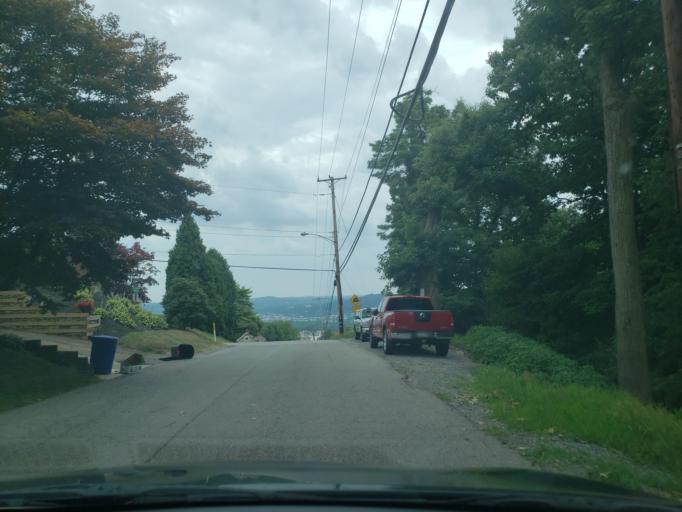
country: US
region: Pennsylvania
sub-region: Allegheny County
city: Avalon
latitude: 40.5081
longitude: -80.0689
